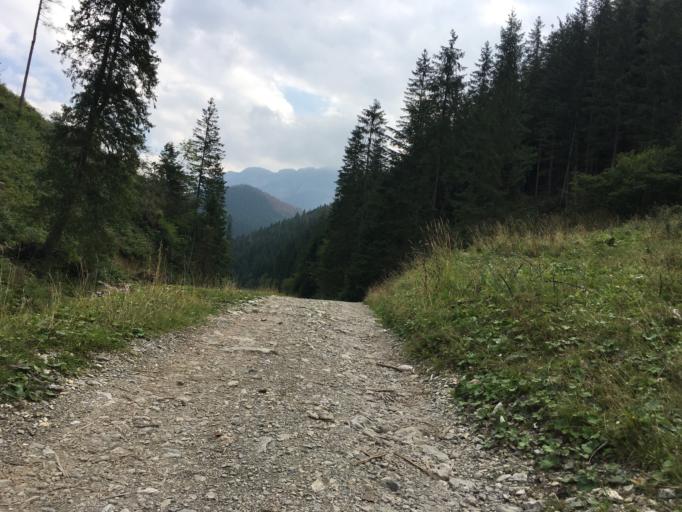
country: PL
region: Lesser Poland Voivodeship
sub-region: Powiat tatrzanski
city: Koscielisko
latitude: 49.2699
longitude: 19.8424
